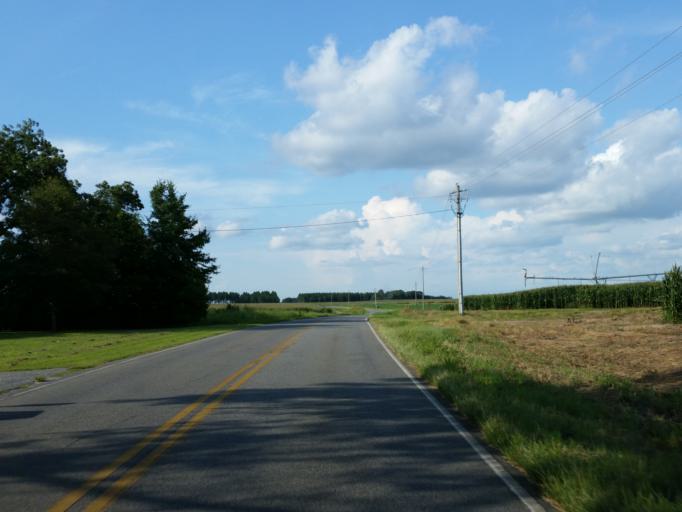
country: US
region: Georgia
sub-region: Crisp County
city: Cordele
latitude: 31.9801
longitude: -83.8741
